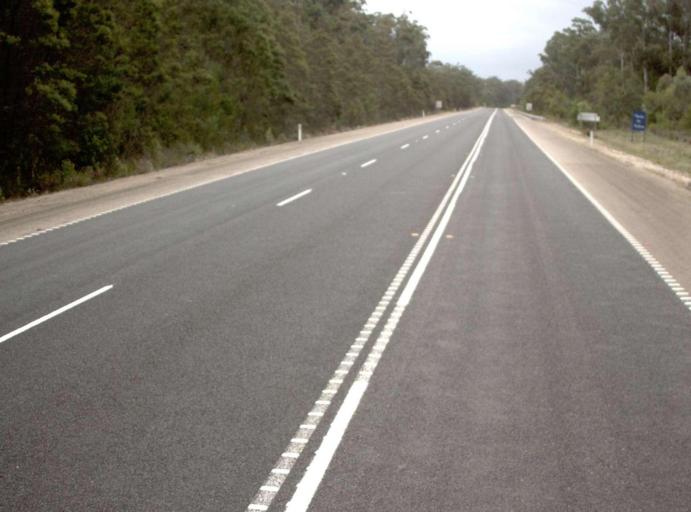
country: AU
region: Victoria
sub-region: East Gippsland
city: Lakes Entrance
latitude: -37.7229
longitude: 148.0850
